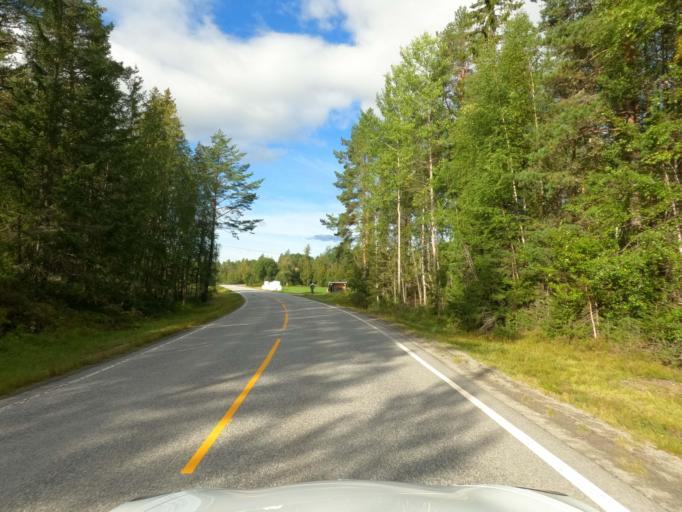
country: NO
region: Telemark
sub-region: Notodden
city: Notodden
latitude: 59.7310
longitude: 9.2484
